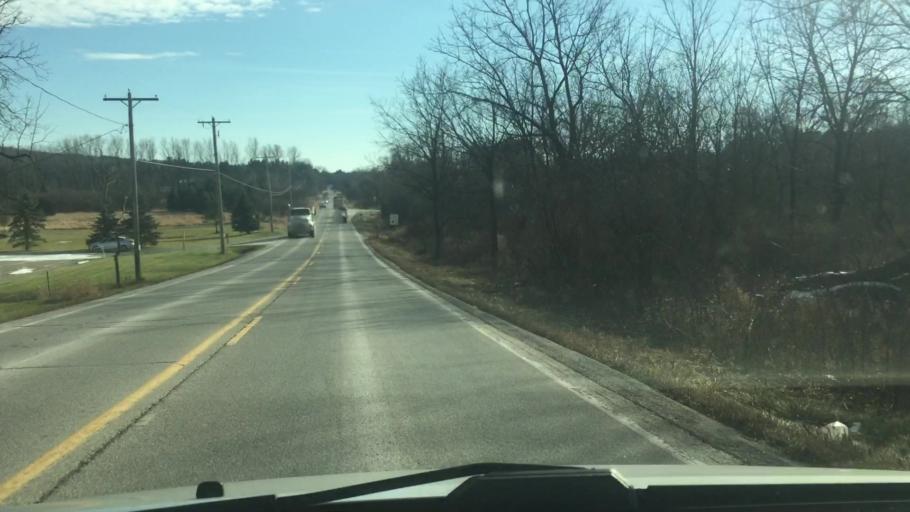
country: US
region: Wisconsin
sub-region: Waukesha County
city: Delafield
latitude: 43.0482
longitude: -88.4044
